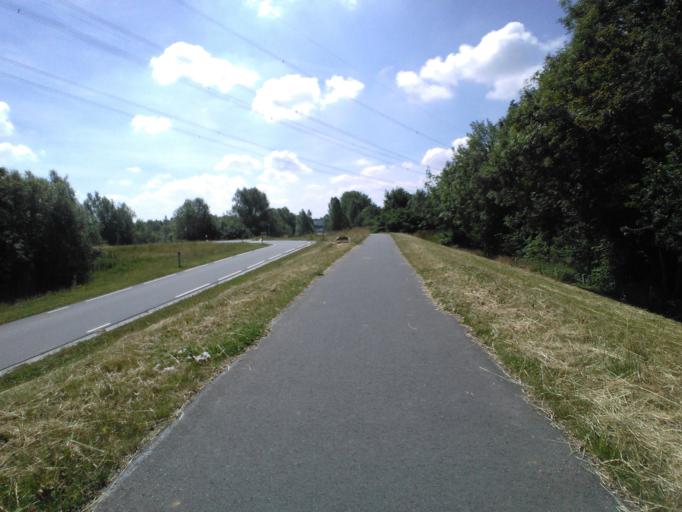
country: NL
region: North Brabant
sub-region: Gemeente Geertruidenberg
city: Geertruidenberg
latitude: 51.7303
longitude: 4.8609
